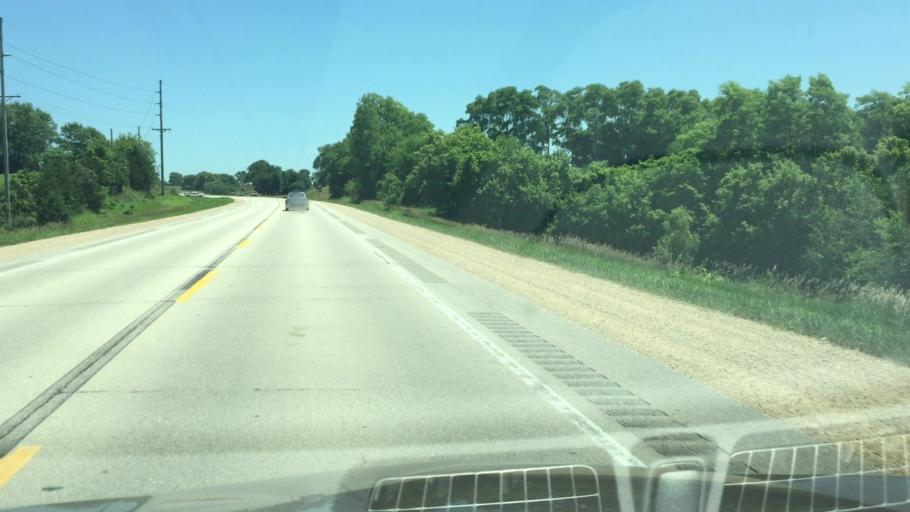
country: US
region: Iowa
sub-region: Jackson County
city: Maquoketa
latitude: 42.0627
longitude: -90.7599
